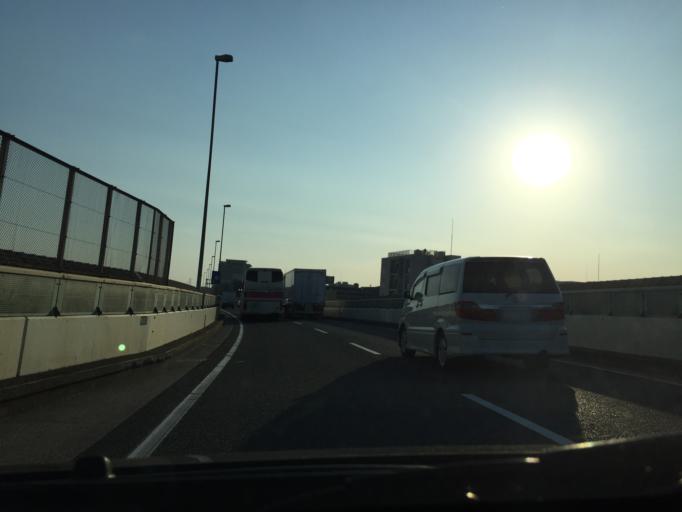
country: JP
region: Kanagawa
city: Yokohama
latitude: 35.4369
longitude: 139.6358
